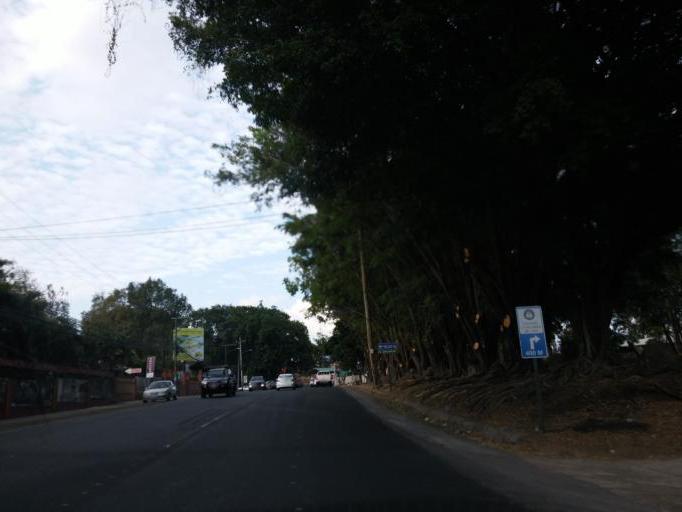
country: CR
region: Heredia
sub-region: Canton de Belen
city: San Antonio
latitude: 9.9769
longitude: -84.1997
